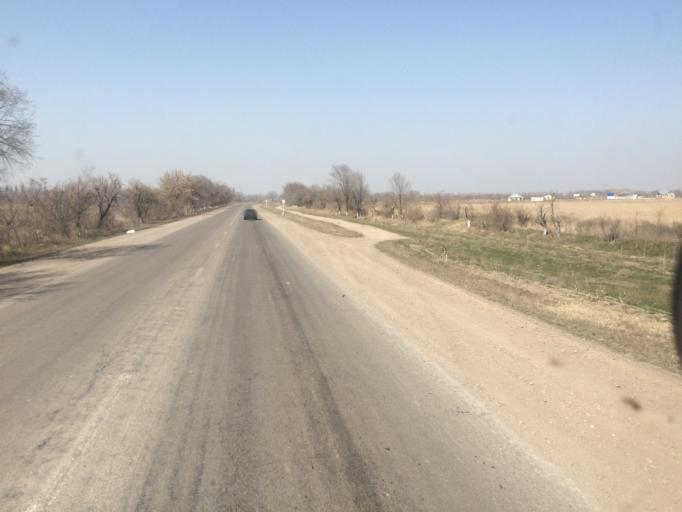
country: KZ
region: Almaty Oblysy
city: Burunday
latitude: 43.3511
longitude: 76.6491
